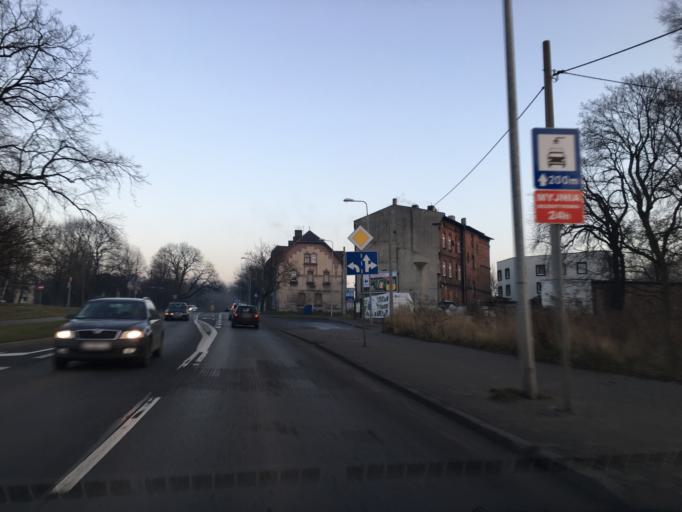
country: PL
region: Silesian Voivodeship
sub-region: Powiat tarnogorski
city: Radzionkow
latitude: 50.3564
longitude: 18.8584
